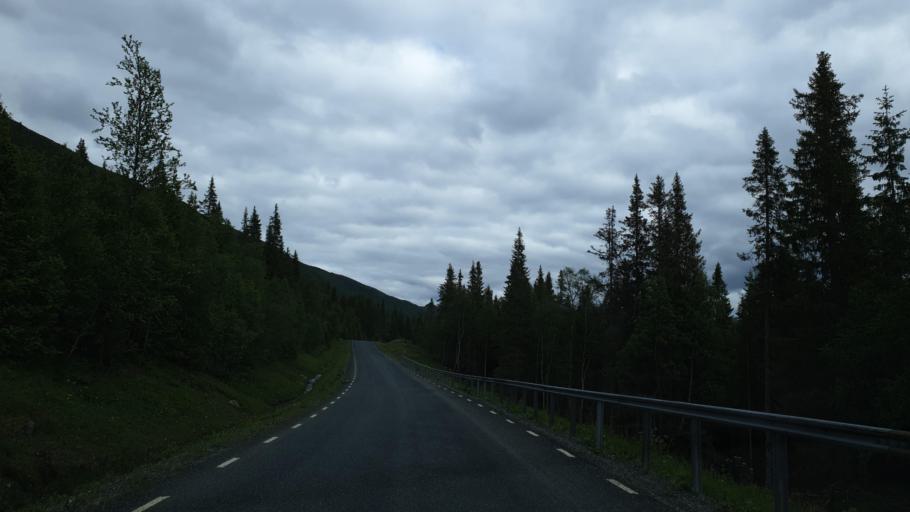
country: NO
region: Nordland
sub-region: Hattfjelldal
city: Hattfjelldal
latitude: 65.4435
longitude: 14.5407
